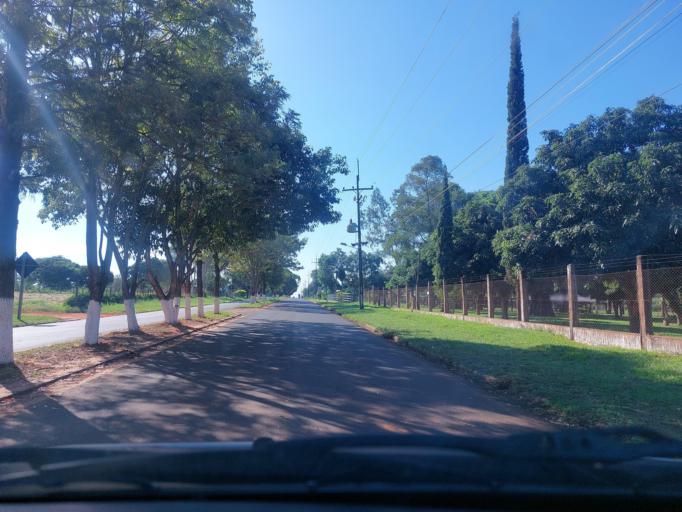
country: PY
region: San Pedro
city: Guayaybi
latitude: -24.5316
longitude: -56.4495
